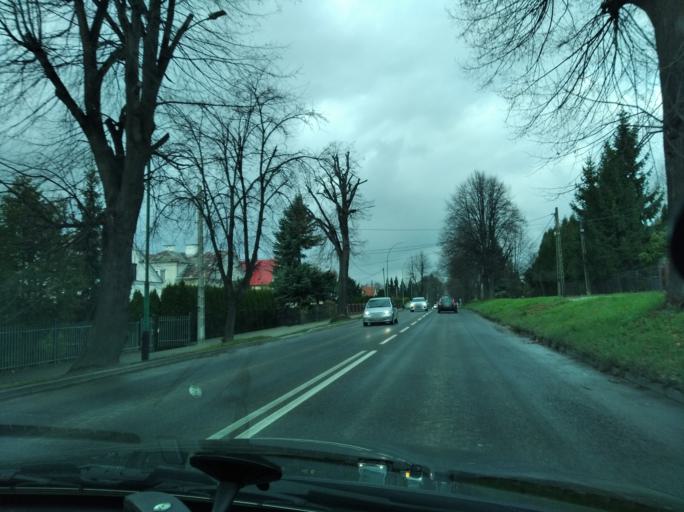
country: PL
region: Subcarpathian Voivodeship
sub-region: Powiat lancucki
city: Lancut
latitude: 50.0740
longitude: 22.2368
